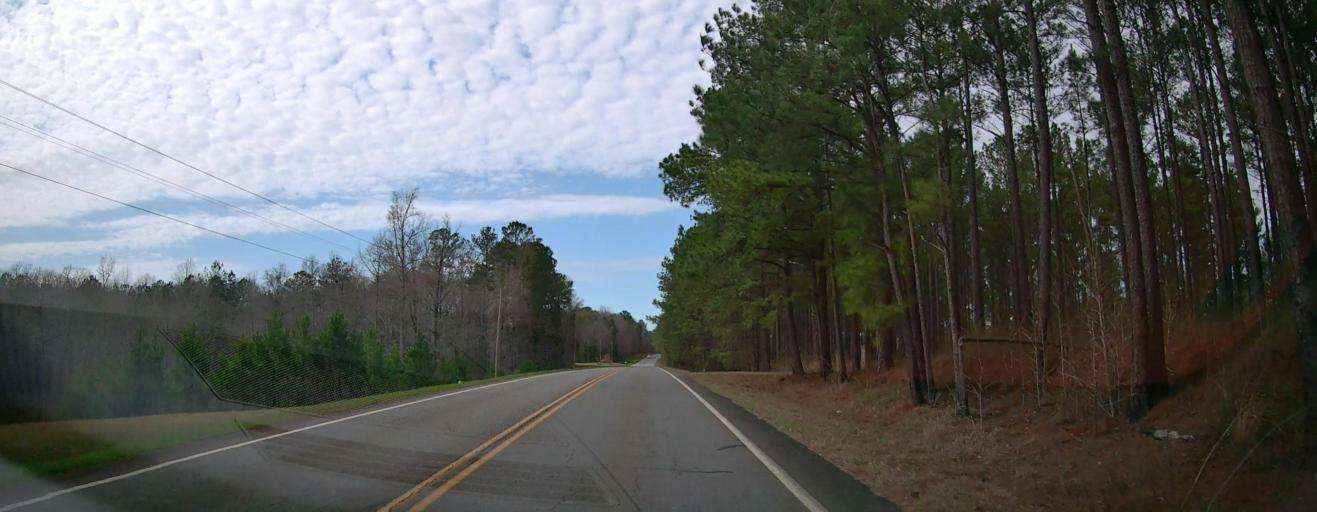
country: US
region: Georgia
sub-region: Jones County
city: Gray
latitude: 33.0001
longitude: -83.6960
